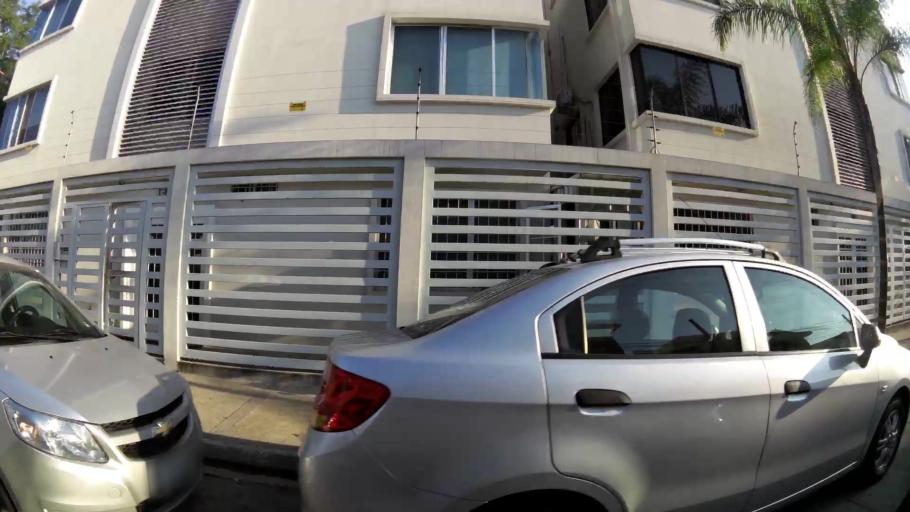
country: EC
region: Guayas
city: Eloy Alfaro
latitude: -2.1627
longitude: -79.8957
